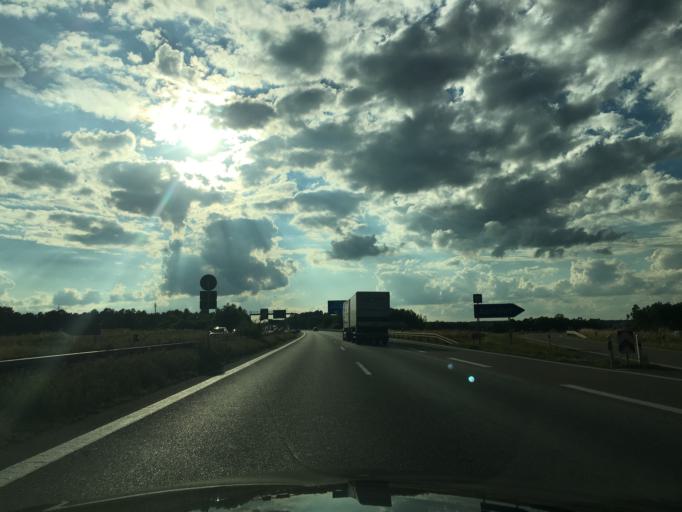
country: DE
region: Bavaria
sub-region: Regierungsbezirk Mittelfranken
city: Burgoberbach
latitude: 49.2562
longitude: 10.5939
